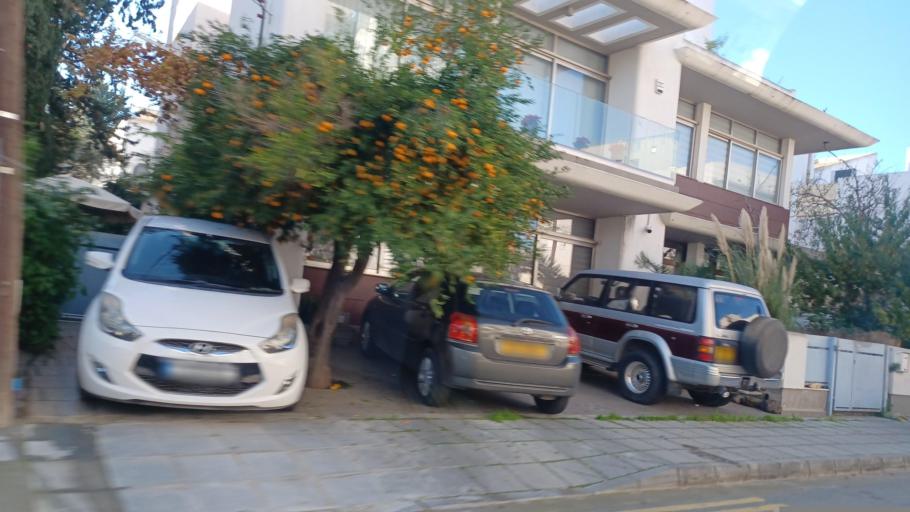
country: CY
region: Lefkosia
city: Nicosia
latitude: 35.1526
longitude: 33.3427
